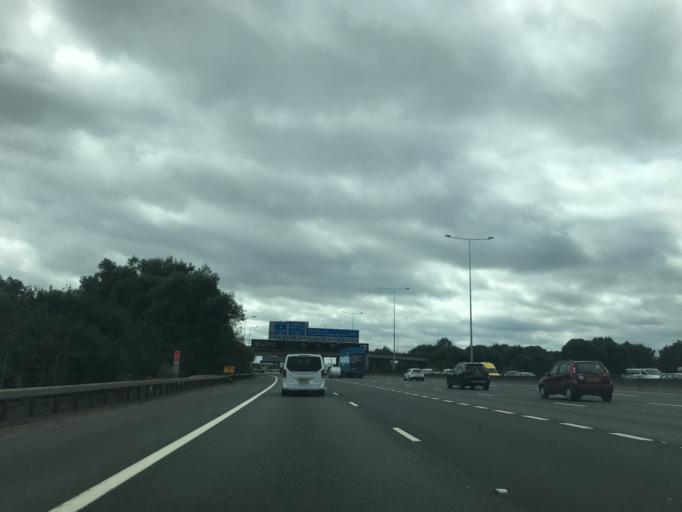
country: GB
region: England
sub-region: Buckinghamshire
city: Iver
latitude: 51.4810
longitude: -0.5024
